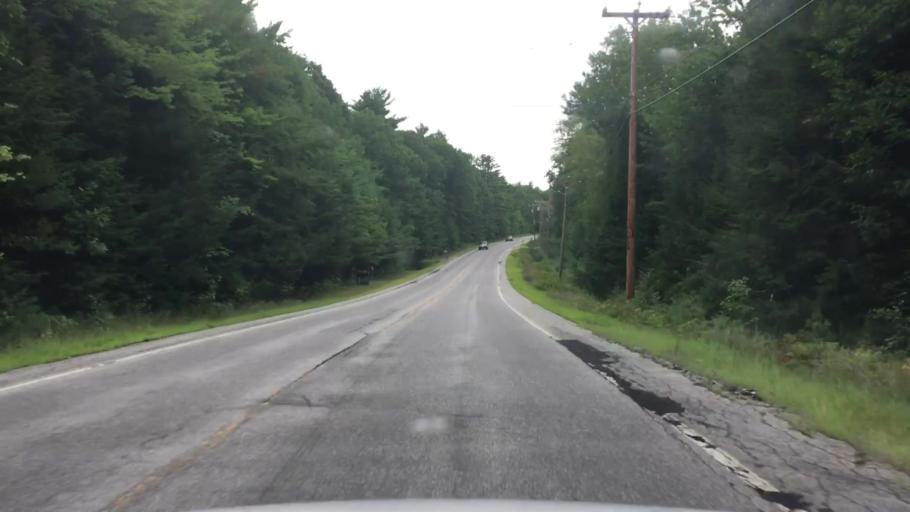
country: US
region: Maine
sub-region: York County
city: Cornish
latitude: 43.8153
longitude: -70.7766
